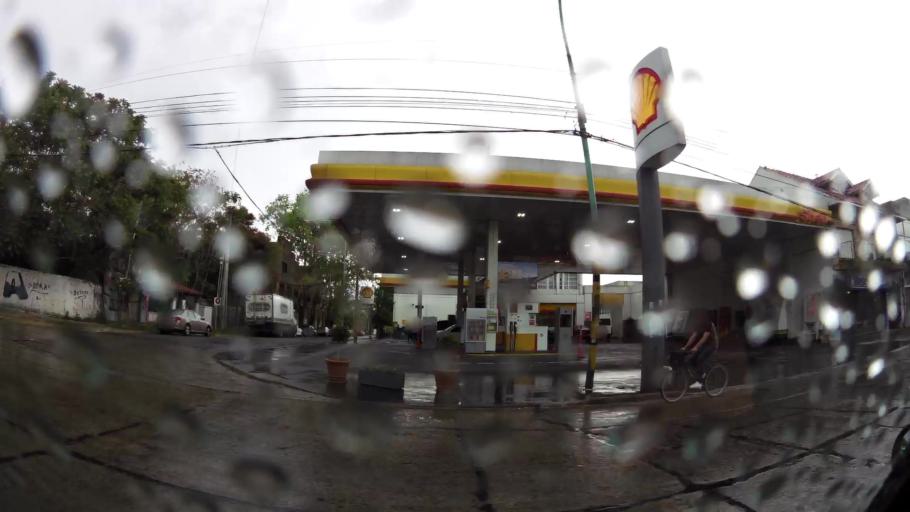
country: AR
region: Buenos Aires
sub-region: Partido de Quilmes
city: Quilmes
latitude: -34.7672
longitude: -58.2198
